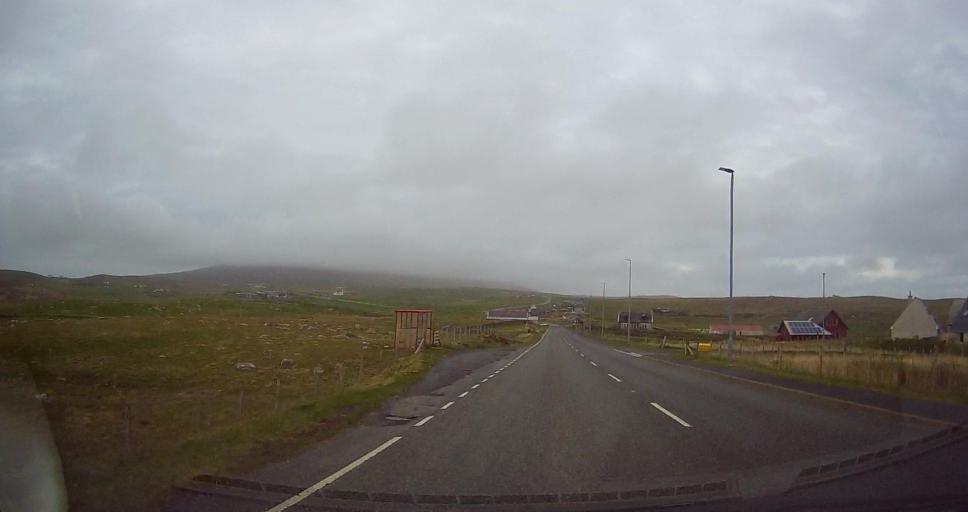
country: GB
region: Scotland
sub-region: Shetland Islands
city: Sandwick
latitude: 59.9220
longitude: -1.2984
